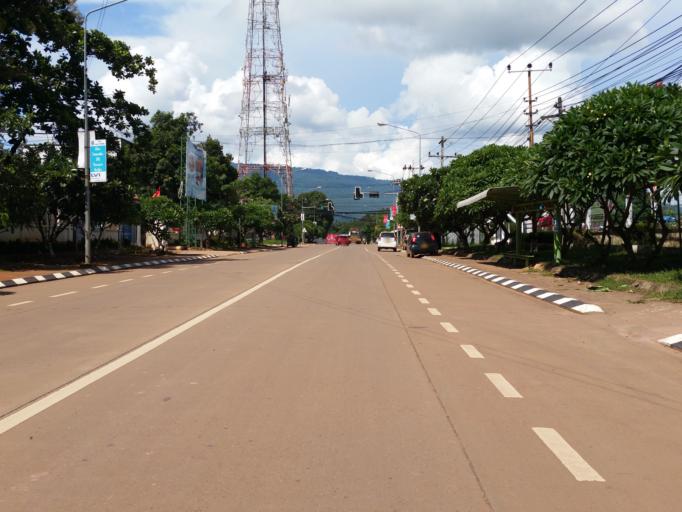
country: LA
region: Champasak
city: Pakxe
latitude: 15.1196
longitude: 105.8050
